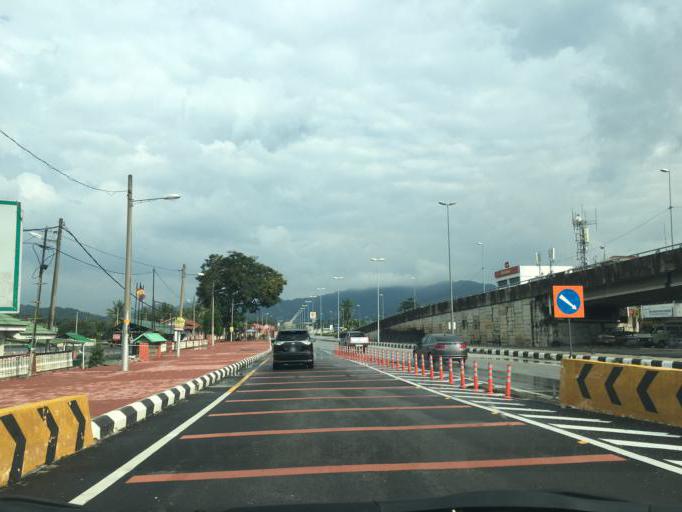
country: MY
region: Selangor
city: Rawang
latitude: 3.3156
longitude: 101.5777
